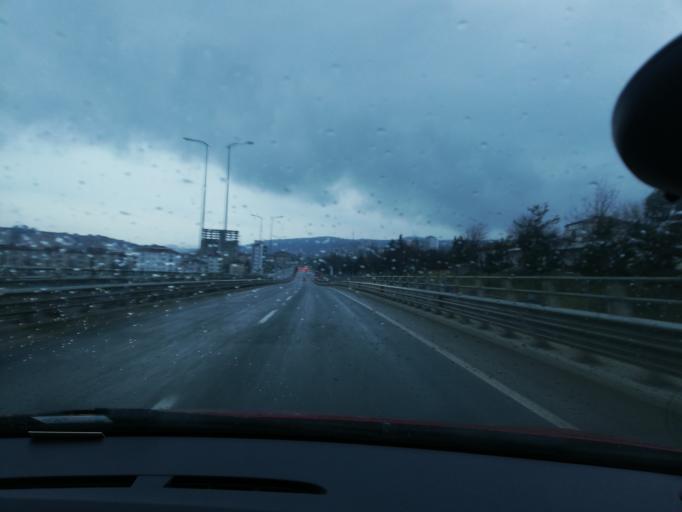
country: TR
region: Kastamonu
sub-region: Cide
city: Kastamonu
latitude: 41.4154
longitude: 33.7963
